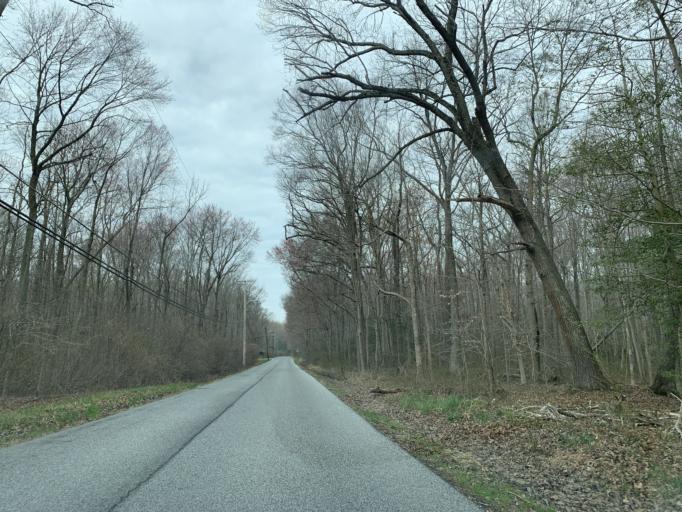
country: US
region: Maryland
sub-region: Baltimore County
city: Edgemere
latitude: 39.2616
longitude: -76.4075
